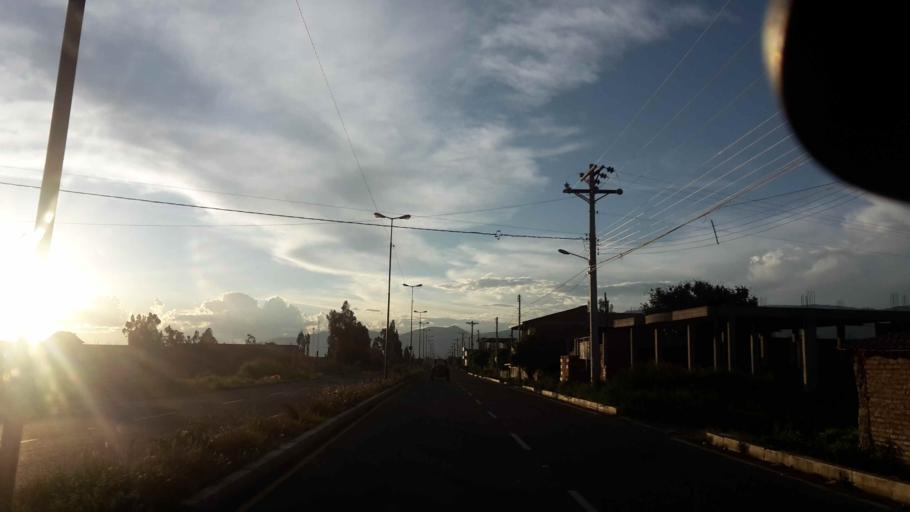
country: BO
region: Cochabamba
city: Punata
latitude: -17.5579
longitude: -65.8056
